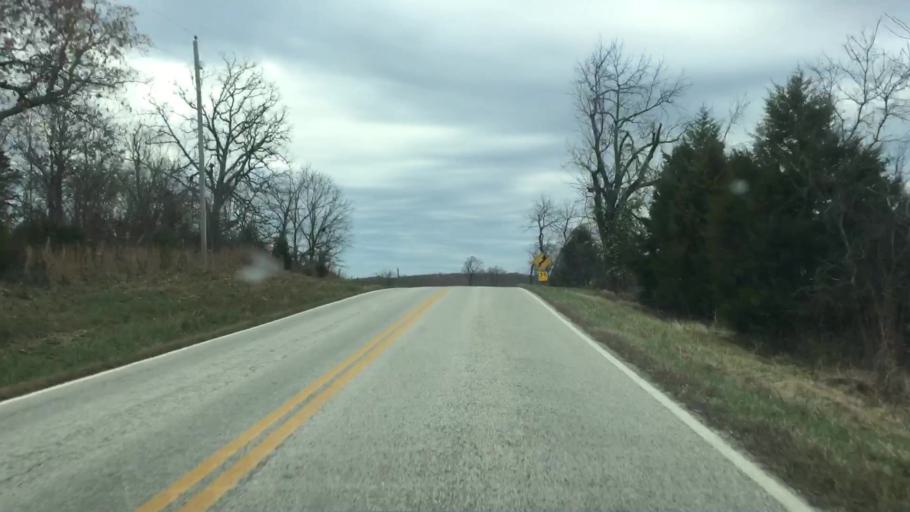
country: US
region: Missouri
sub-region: Saint Clair County
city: Osceola
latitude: 37.9891
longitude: -93.6182
